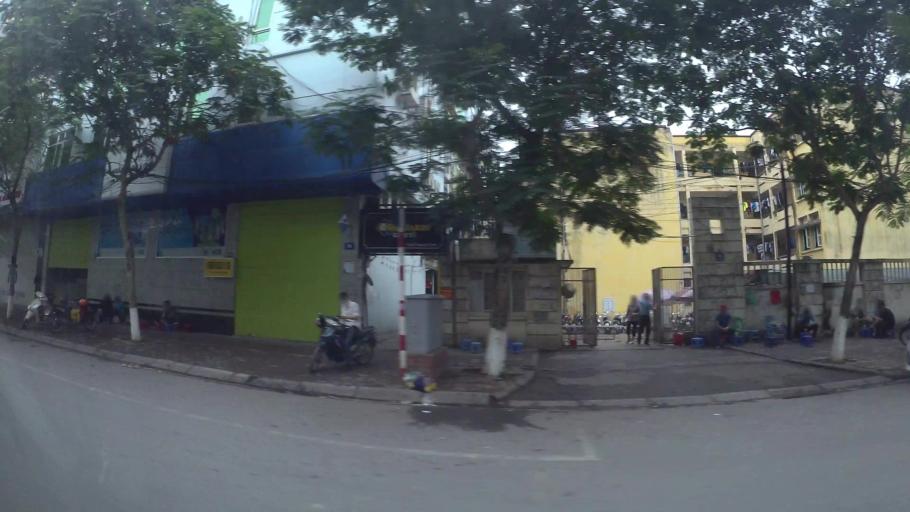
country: VN
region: Ha Noi
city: Hai BaTrung
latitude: 21.0005
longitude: 105.8452
